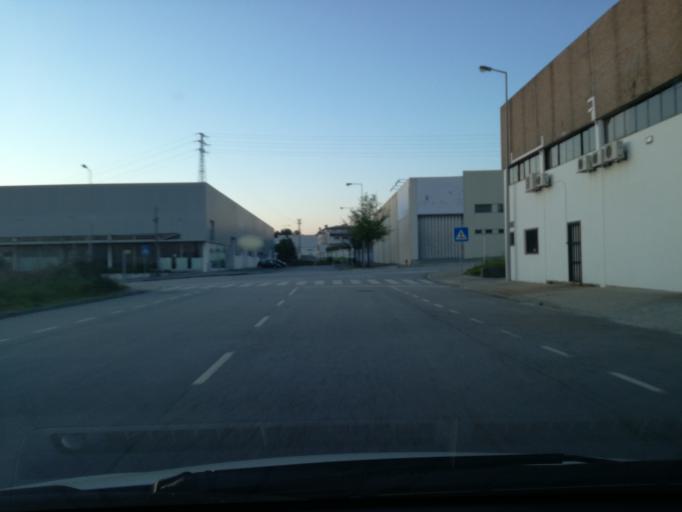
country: PT
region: Porto
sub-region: Maia
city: Gemunde
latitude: 41.2561
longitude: -8.6413
